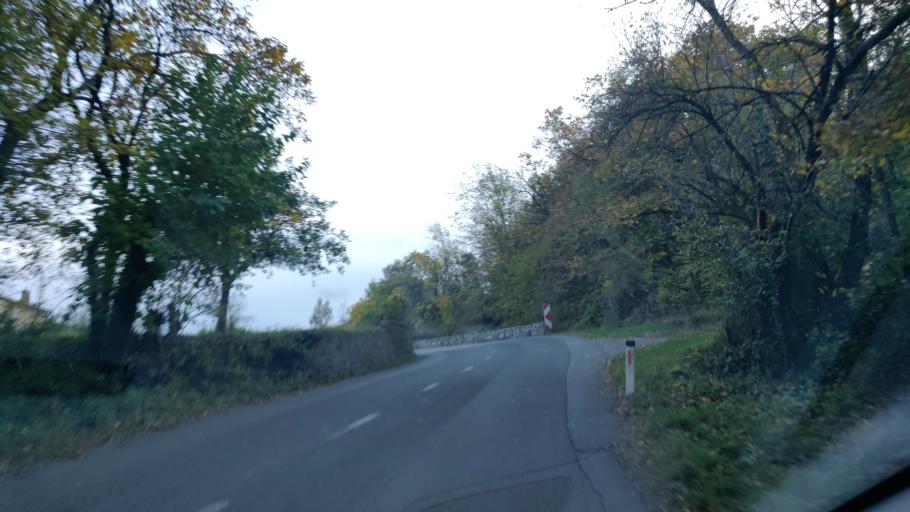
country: SI
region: Sezana
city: Sezana
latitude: 45.7886
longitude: 13.8619
